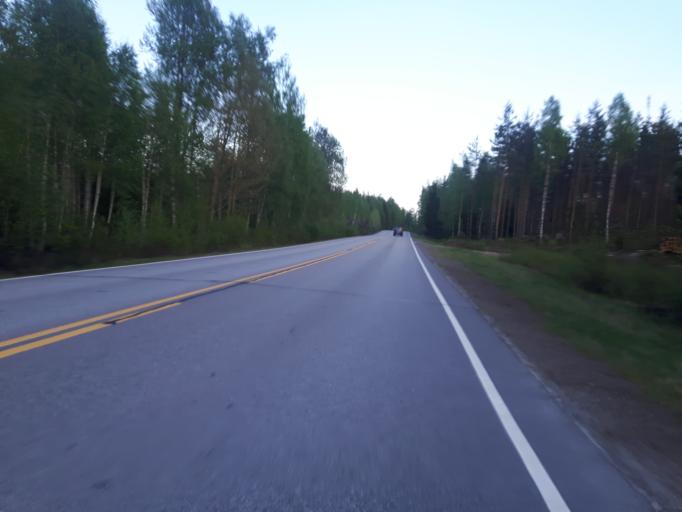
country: FI
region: Uusimaa
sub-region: Loviisa
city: Perna
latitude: 60.4586
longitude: 26.0740
